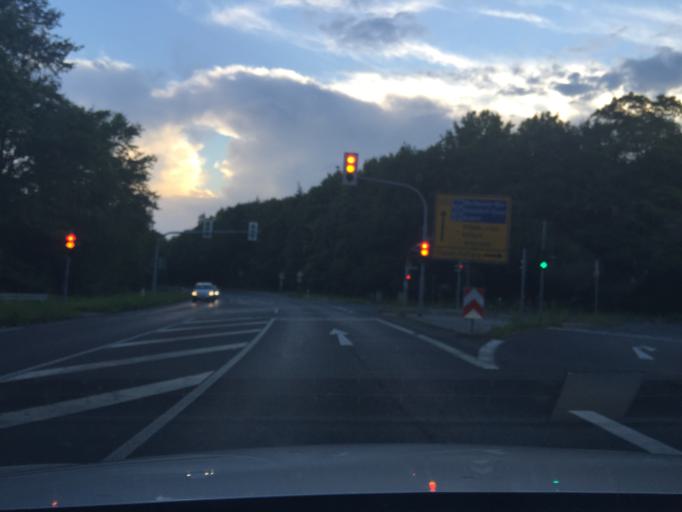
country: DE
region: North Rhine-Westphalia
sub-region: Regierungsbezirk Dusseldorf
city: Ratingen
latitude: 51.3451
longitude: 6.8849
